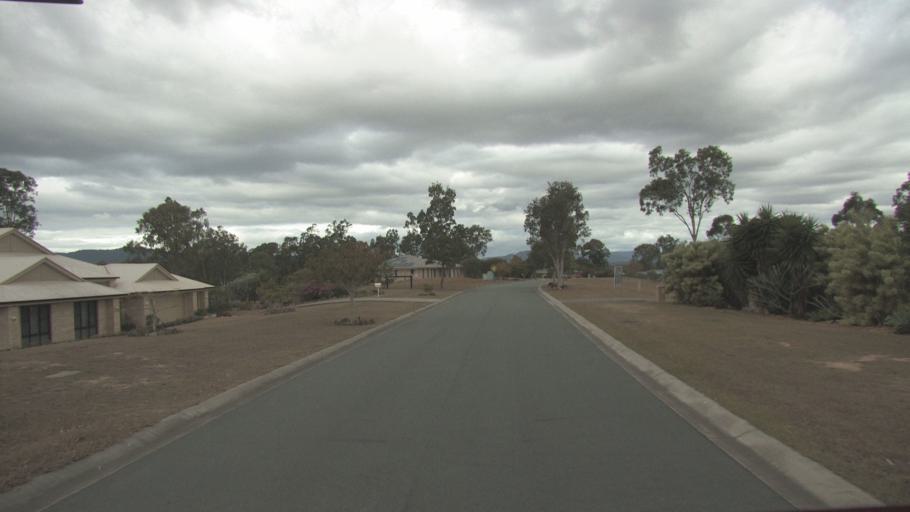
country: AU
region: Queensland
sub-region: Logan
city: Cedar Vale
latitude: -27.8727
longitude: 153.0740
